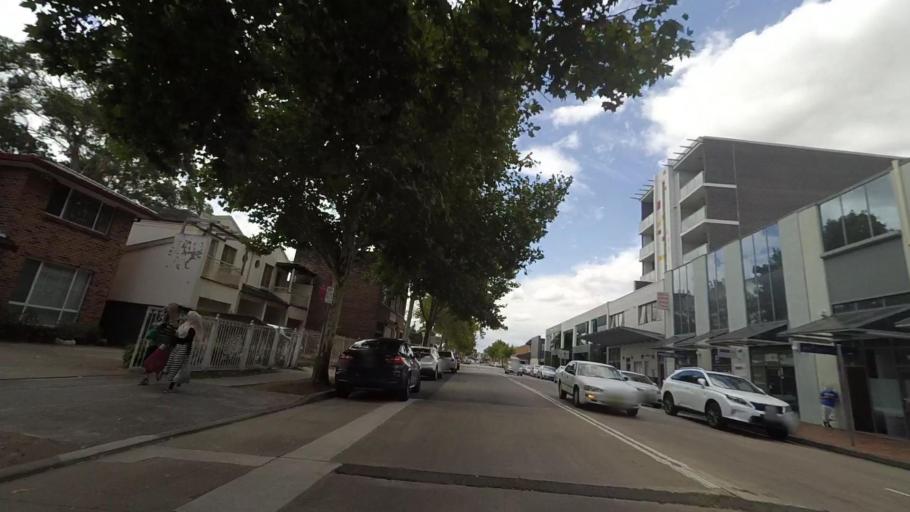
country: AU
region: New South Wales
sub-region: Fairfield
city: Carramar
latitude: -33.8733
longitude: 150.9530
